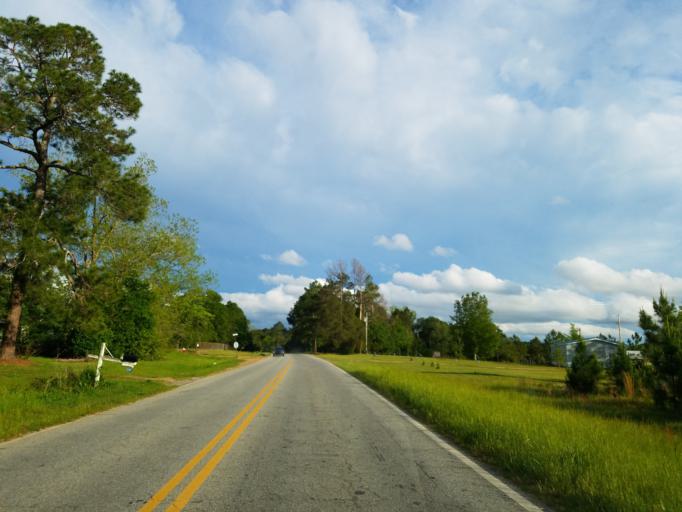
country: US
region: Georgia
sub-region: Crisp County
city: Cordele
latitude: 31.9363
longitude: -83.7845
